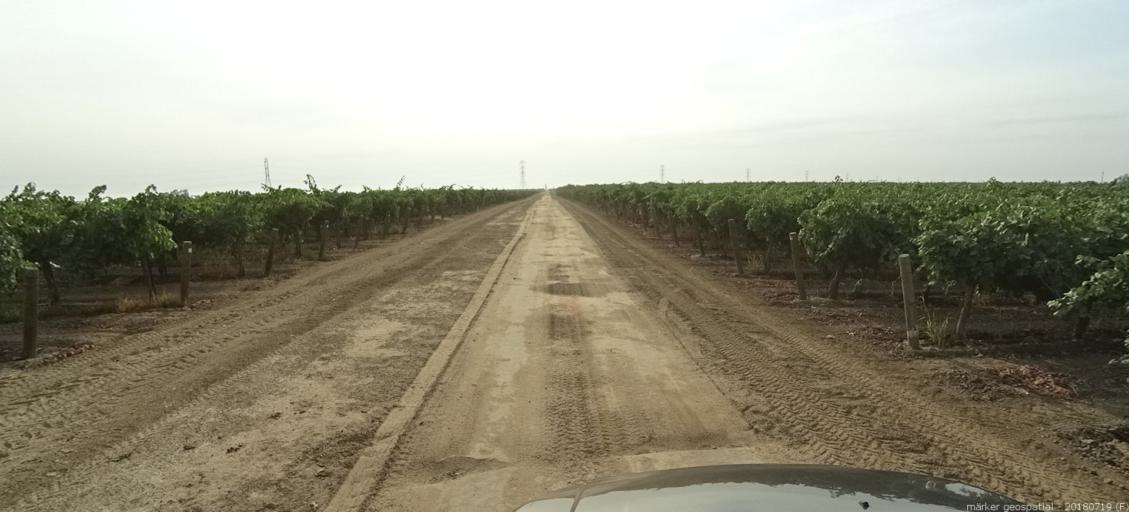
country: US
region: California
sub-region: Madera County
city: Fairmead
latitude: 37.1127
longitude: -120.1961
